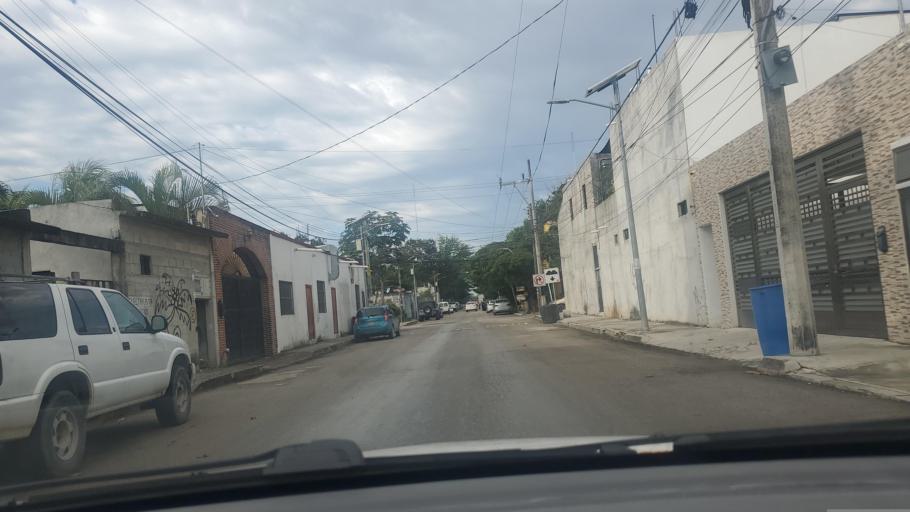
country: MX
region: Quintana Roo
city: Tulum
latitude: 20.2124
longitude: -87.4636
